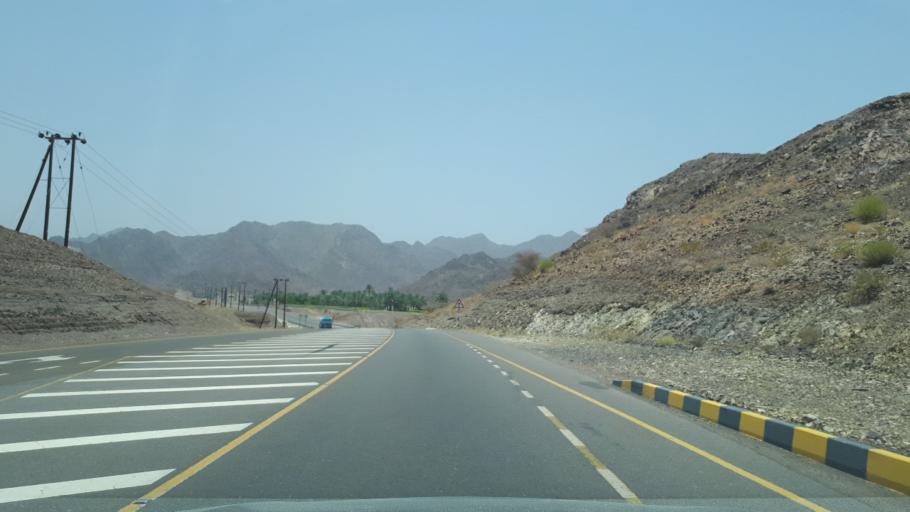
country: OM
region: Al Batinah
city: Rustaq
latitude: 23.4276
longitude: 57.2844
